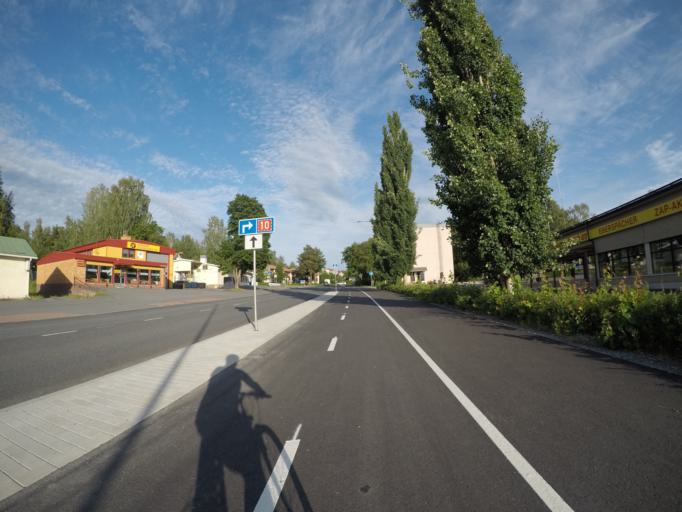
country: FI
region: Haeme
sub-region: Haemeenlinna
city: Haemeenlinna
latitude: 60.9846
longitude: 24.4432
